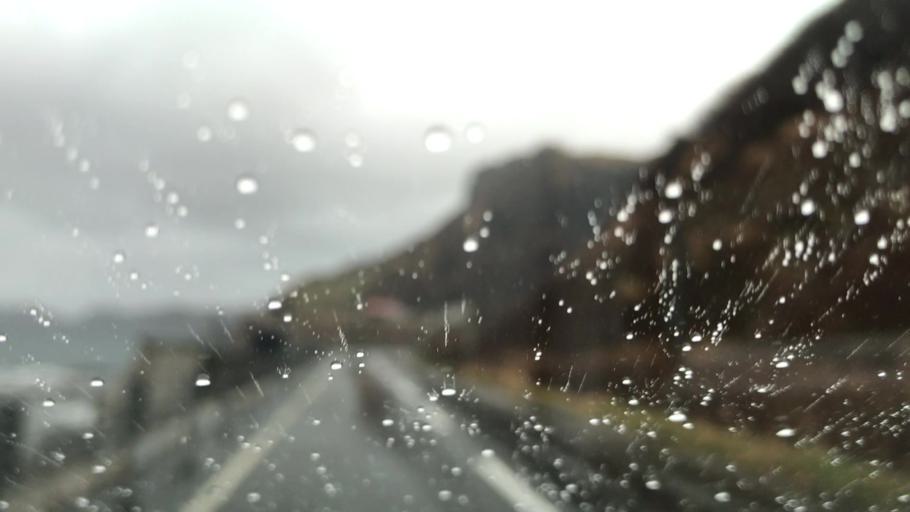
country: JP
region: Hokkaido
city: Iwanai
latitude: 43.2999
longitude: 140.3543
